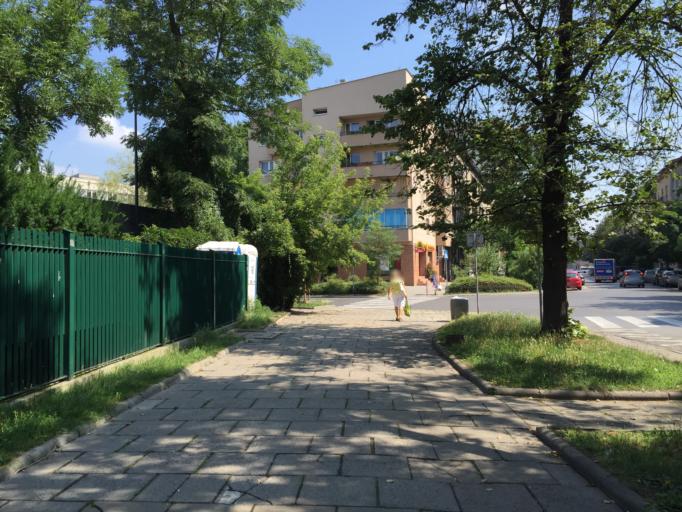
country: PL
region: Lesser Poland Voivodeship
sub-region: Krakow
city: Krakow
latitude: 50.0571
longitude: 19.9226
